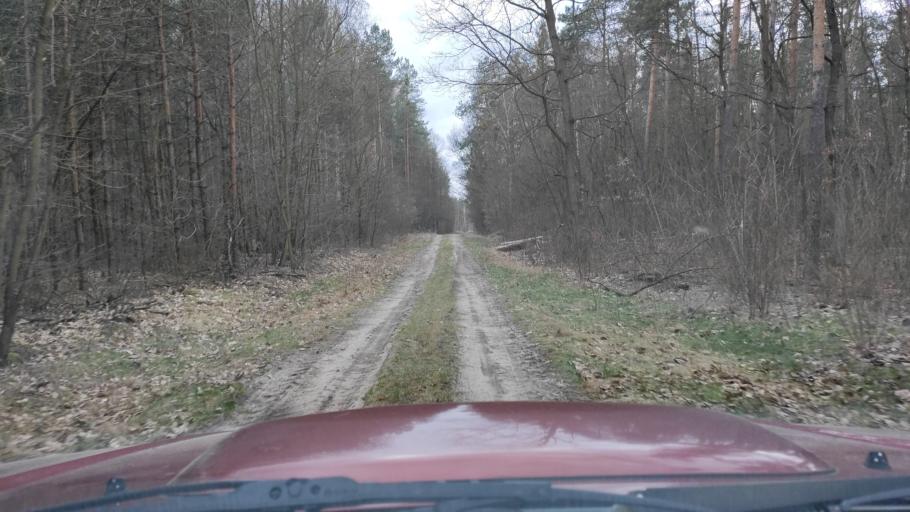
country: PL
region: Masovian Voivodeship
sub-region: Powiat kozienicki
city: Garbatka-Letnisko
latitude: 51.5094
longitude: 21.5476
